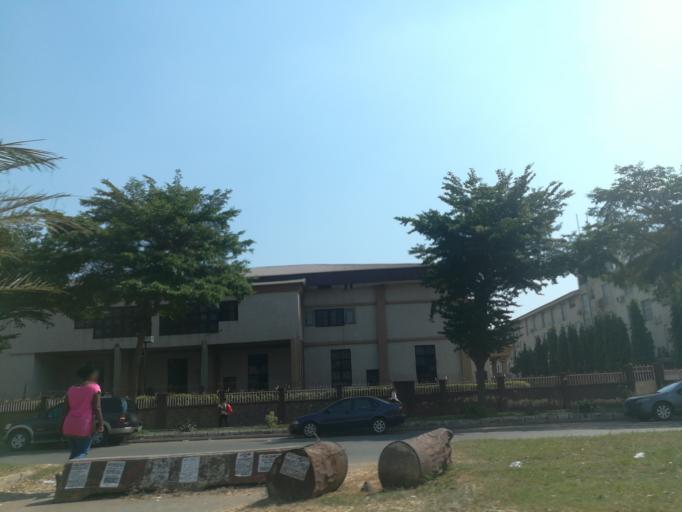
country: NG
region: Abuja Federal Capital Territory
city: Abuja
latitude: 9.0678
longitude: 7.4405
